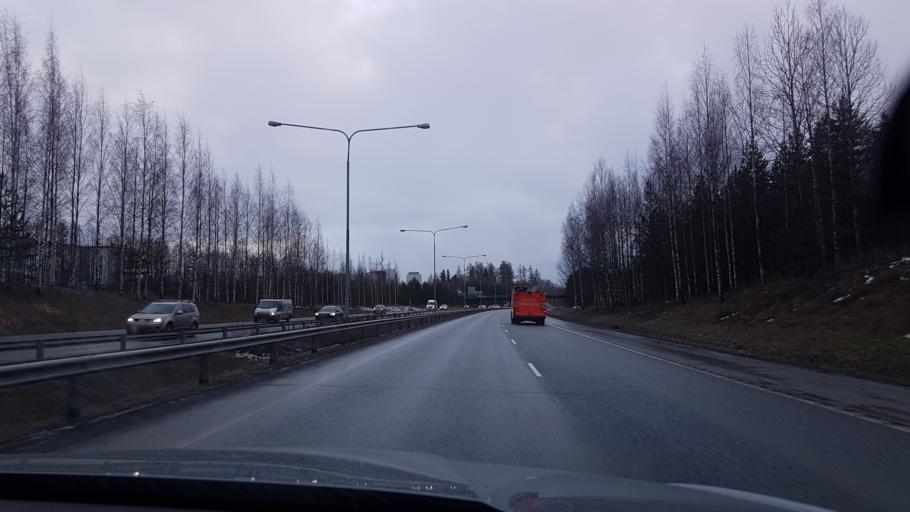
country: FI
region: Pirkanmaa
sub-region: Tampere
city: Tampere
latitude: 61.4771
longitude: 23.8701
